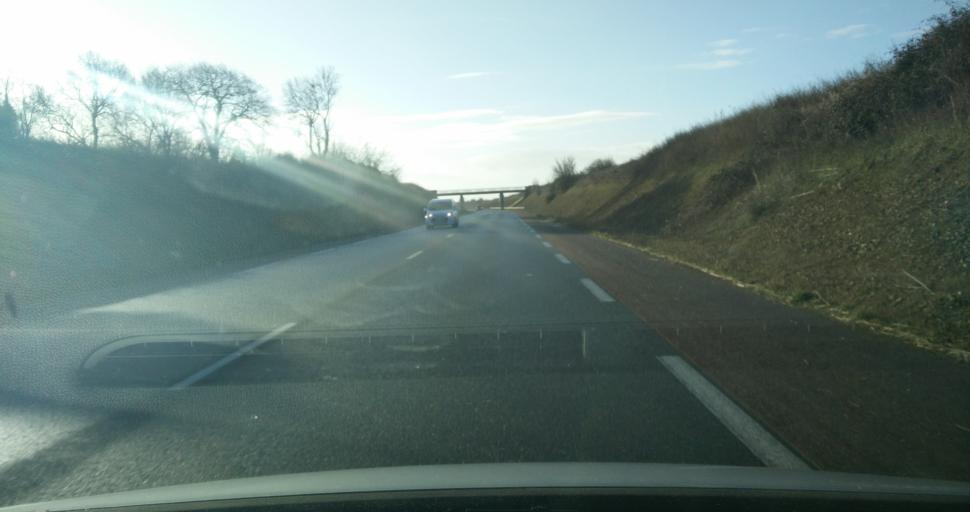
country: FR
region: Poitou-Charentes
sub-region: Departement de la Charente-Maritime
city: Saint-Xandre
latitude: 46.1875
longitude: -1.0937
